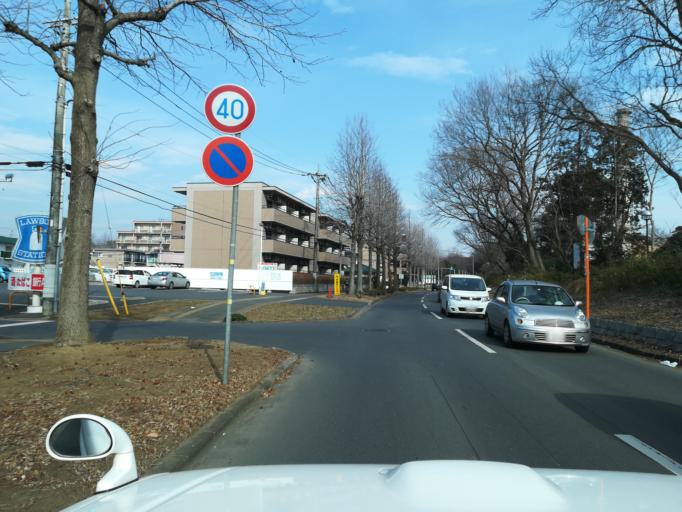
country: JP
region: Ibaraki
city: Naka
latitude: 36.0945
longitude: 140.0983
